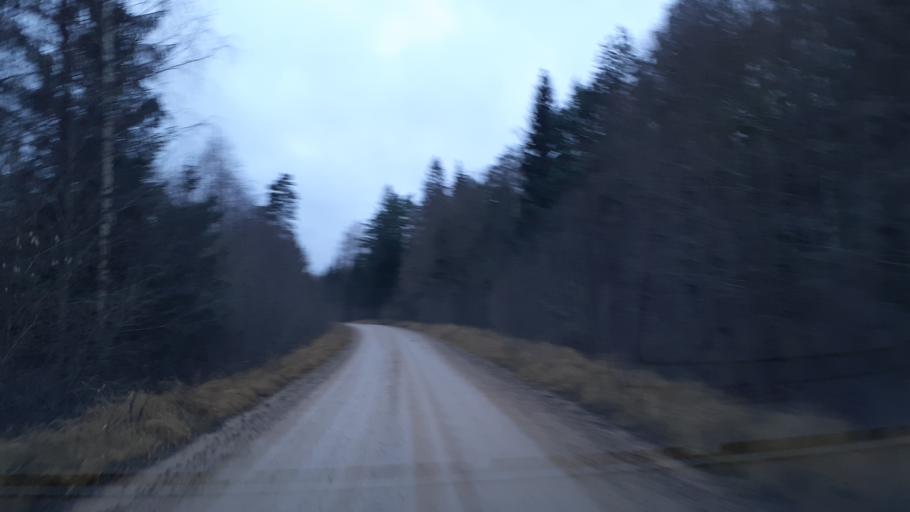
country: LV
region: Kuldigas Rajons
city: Kuldiga
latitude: 57.0547
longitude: 22.1143
